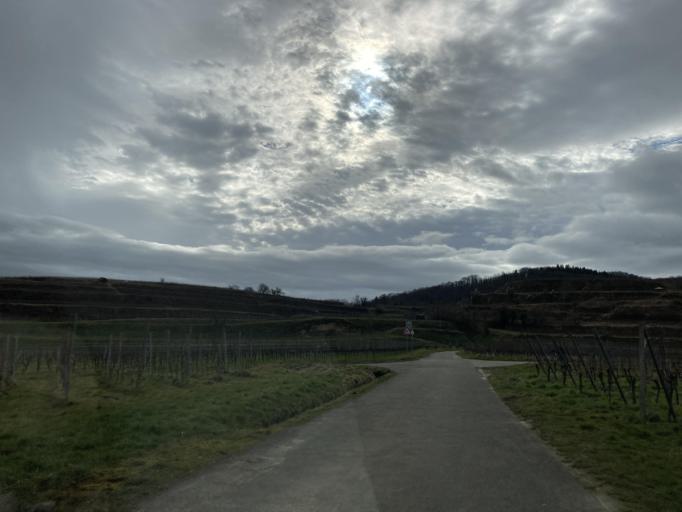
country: DE
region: Baden-Wuerttemberg
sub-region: Freiburg Region
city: Endingen
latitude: 48.1306
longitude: 7.7044
